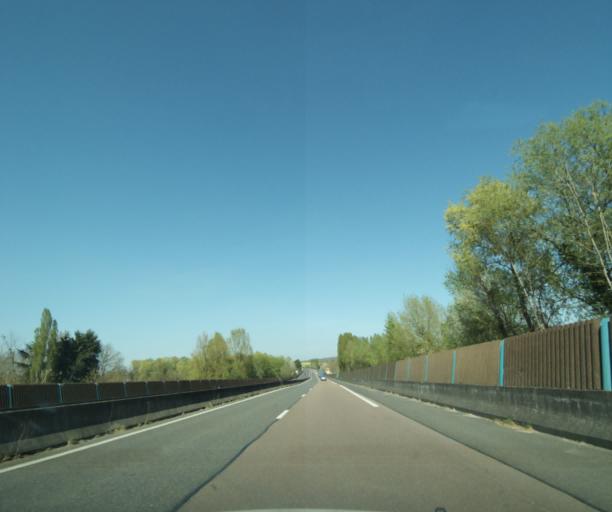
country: FR
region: Bourgogne
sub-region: Departement de la Nievre
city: Cosne-Cours-sur-Loire
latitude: 47.4017
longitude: 2.9405
